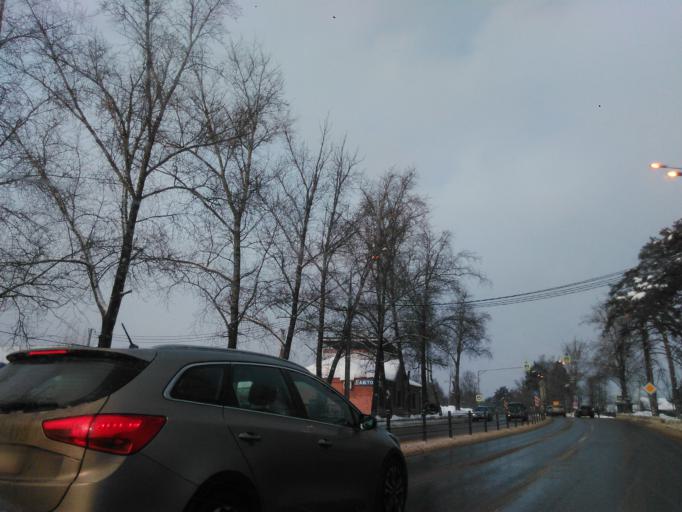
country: RU
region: Moskovskaya
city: Dedenevo
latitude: 56.2331
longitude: 37.5267
